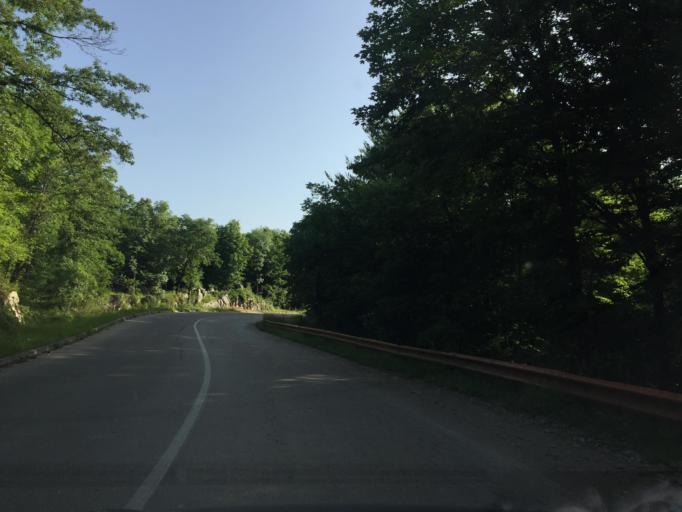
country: HR
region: Primorsko-Goranska
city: Kastav
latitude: 45.4220
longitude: 14.3242
